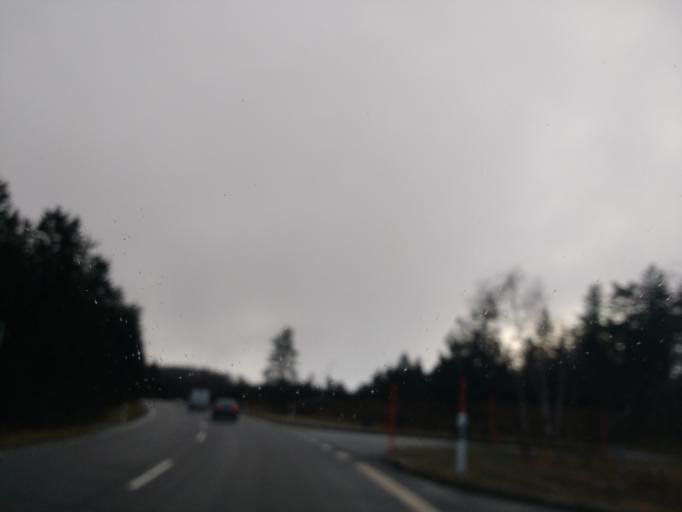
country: DE
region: Baden-Wuerttemberg
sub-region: Freiburg Region
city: Seebach
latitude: 48.5285
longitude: 8.2154
